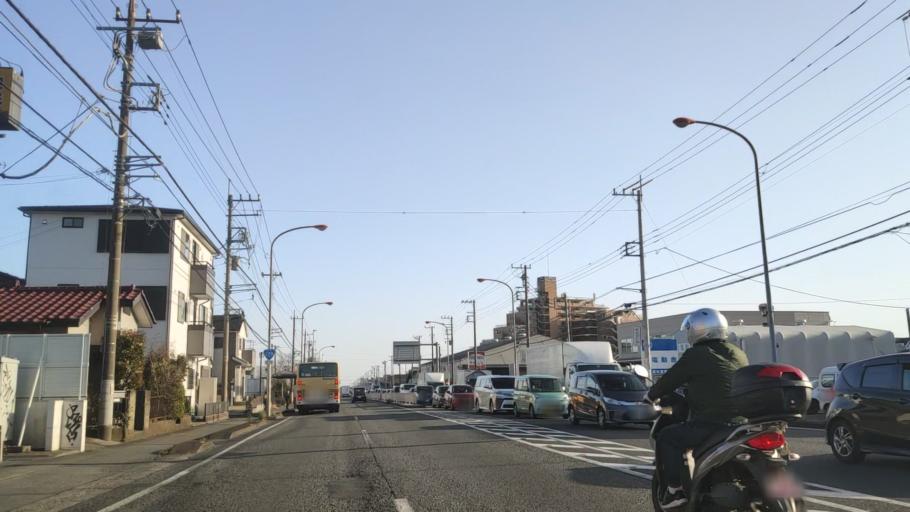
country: JP
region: Kanagawa
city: Zama
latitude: 35.4852
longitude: 139.3652
